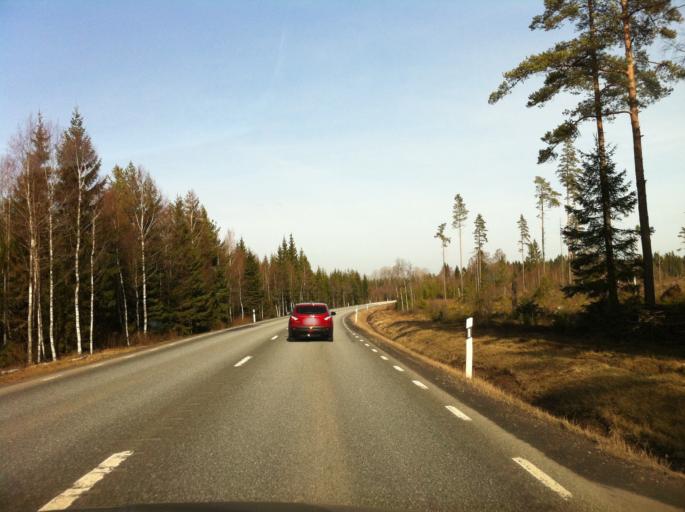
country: SE
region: Joenkoeping
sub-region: Mullsjo Kommun
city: Mullsjoe
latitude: 58.0248
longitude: 13.8310
